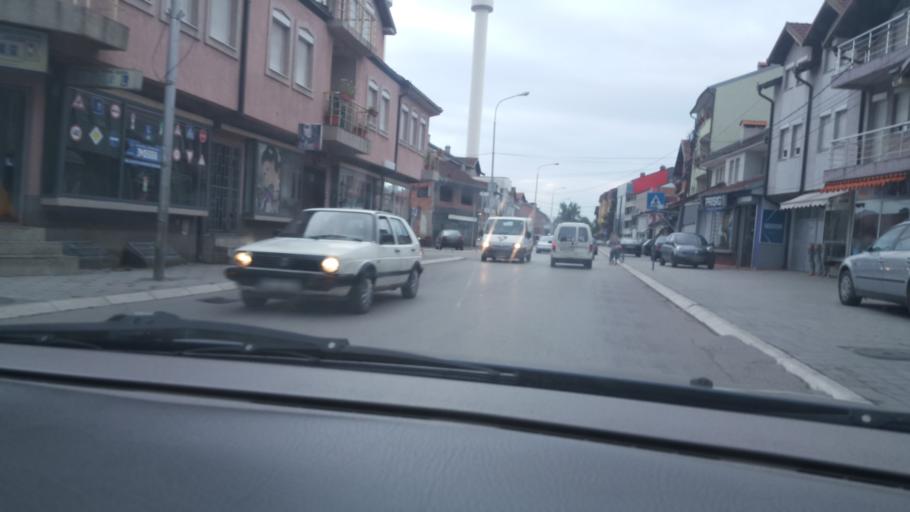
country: XK
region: Gjakova
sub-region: Komuna e Gjakoves
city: Gjakove
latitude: 42.3902
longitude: 20.4261
